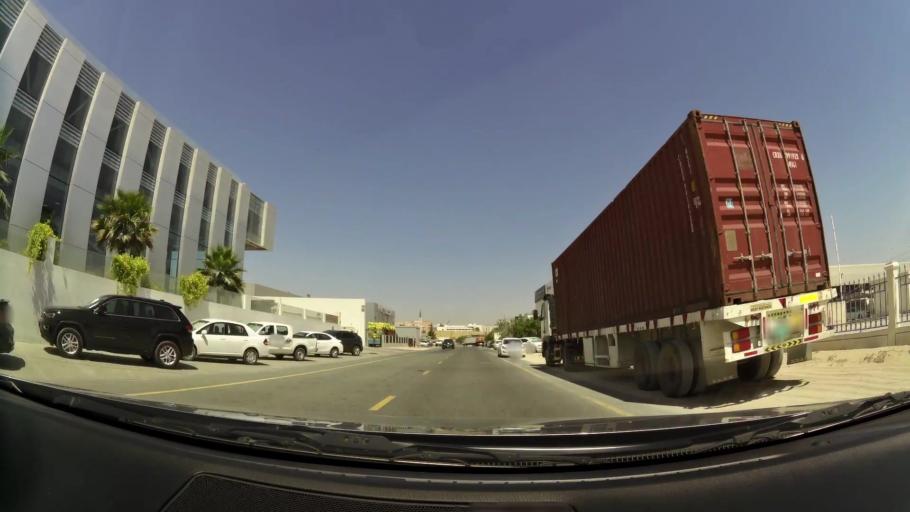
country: AE
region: Dubai
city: Dubai
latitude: 24.9875
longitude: 55.2095
